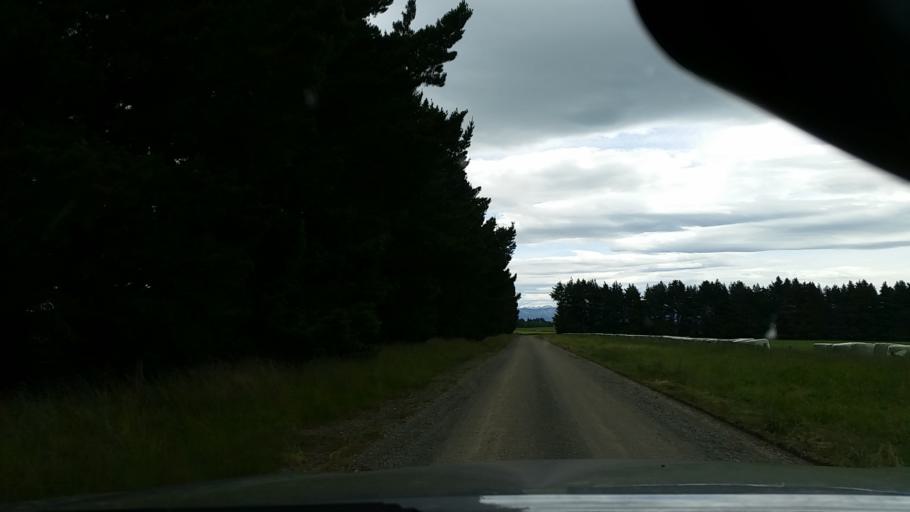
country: NZ
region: Otago
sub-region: Queenstown-Lakes District
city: Kingston
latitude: -45.6281
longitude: 168.3482
